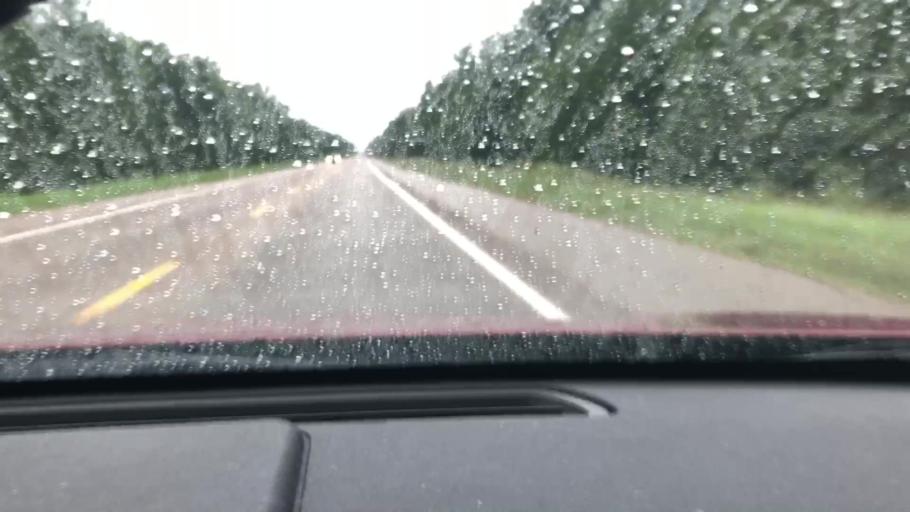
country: US
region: Arkansas
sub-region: Columbia County
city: Magnolia
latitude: 33.2998
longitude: -93.2654
